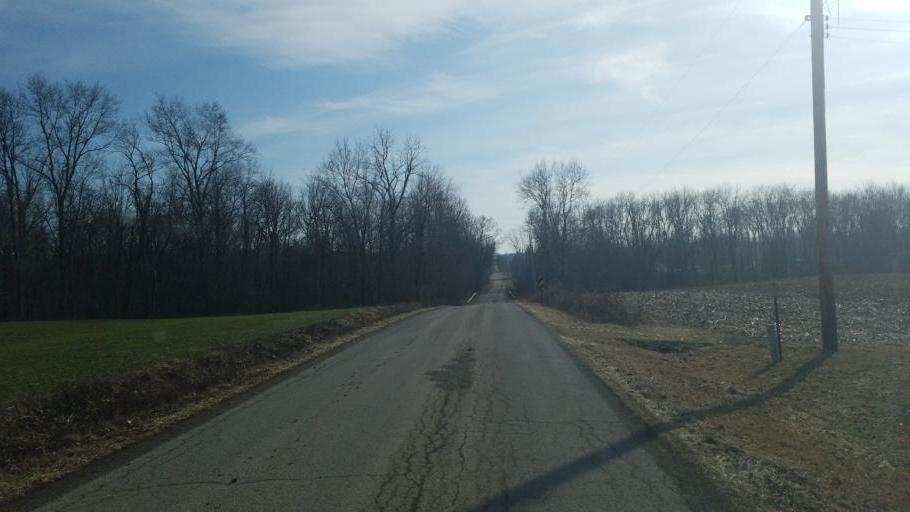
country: US
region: Ohio
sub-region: Crawford County
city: Crestline
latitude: 40.7064
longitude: -82.6892
